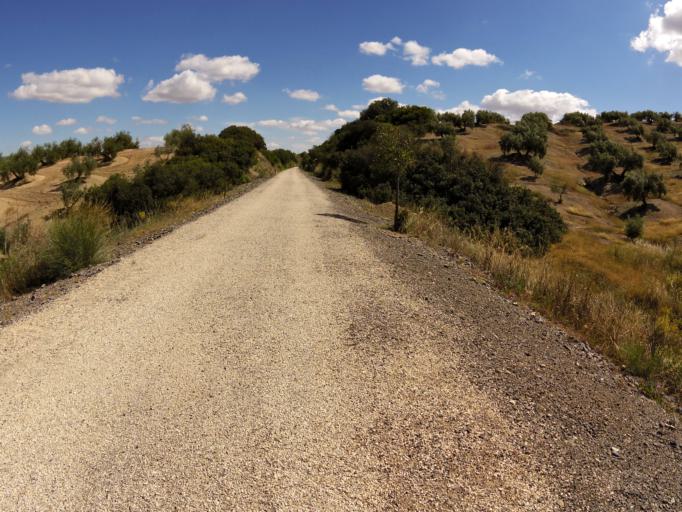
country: ES
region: Andalusia
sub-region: Provincia de Jaen
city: Alcaudete
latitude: 37.6274
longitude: -4.0896
